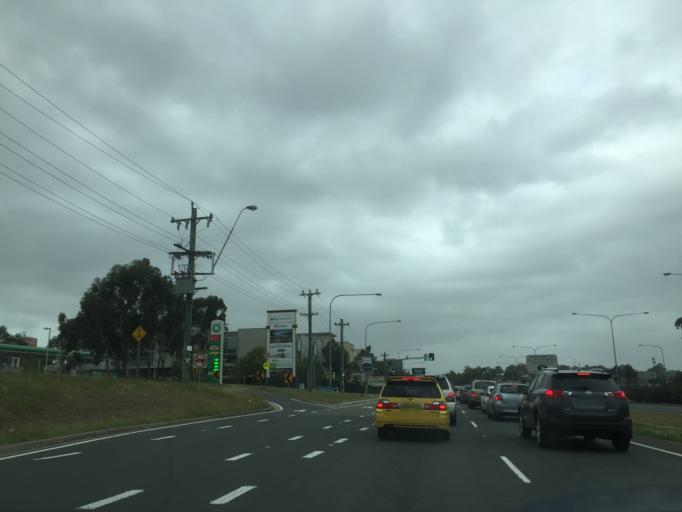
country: AU
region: New South Wales
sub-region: Blacktown
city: Stanhope Gardens
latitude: -33.7318
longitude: 150.9430
